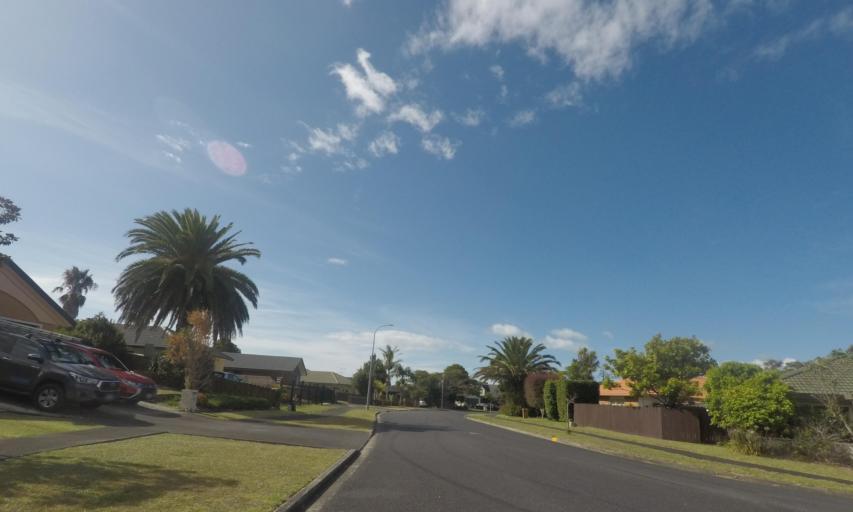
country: NZ
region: Auckland
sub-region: Auckland
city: Pakuranga
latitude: -36.9229
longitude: 174.8919
